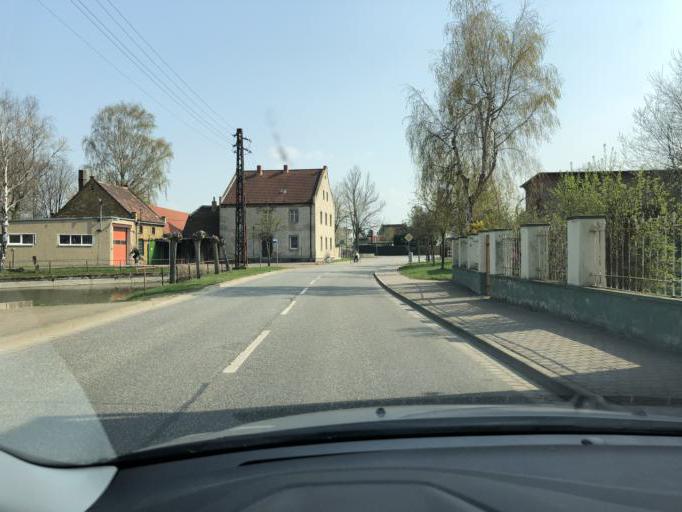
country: DE
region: Saxony-Anhalt
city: Hohenthurm
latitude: 51.4997
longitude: 12.0989
